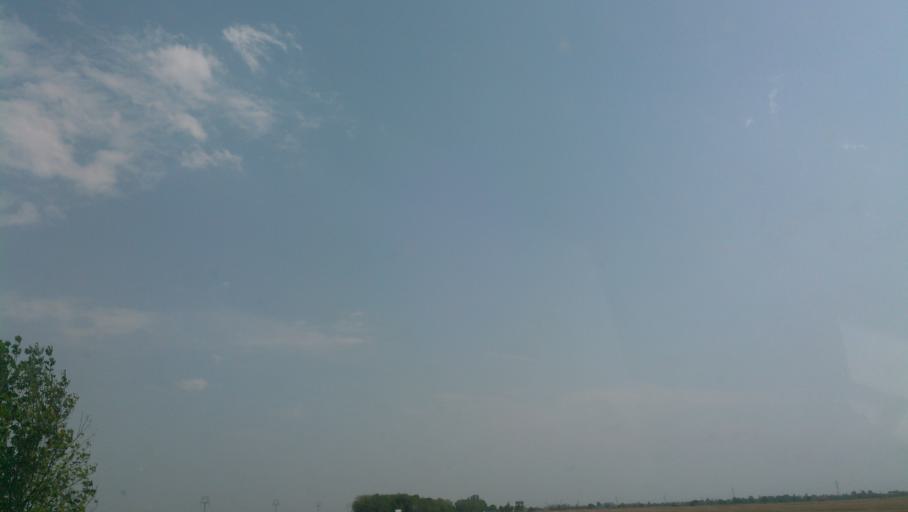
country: SK
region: Trnavsky
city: Samorin
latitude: 48.0902
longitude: 17.3742
